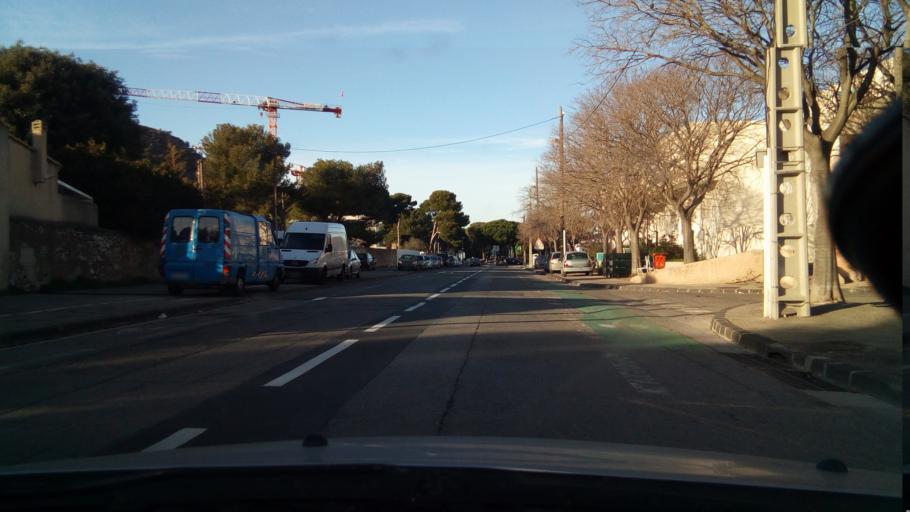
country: FR
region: Provence-Alpes-Cote d'Azur
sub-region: Departement des Bouches-du-Rhone
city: Marseille 09
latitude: 43.2305
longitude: 5.4010
